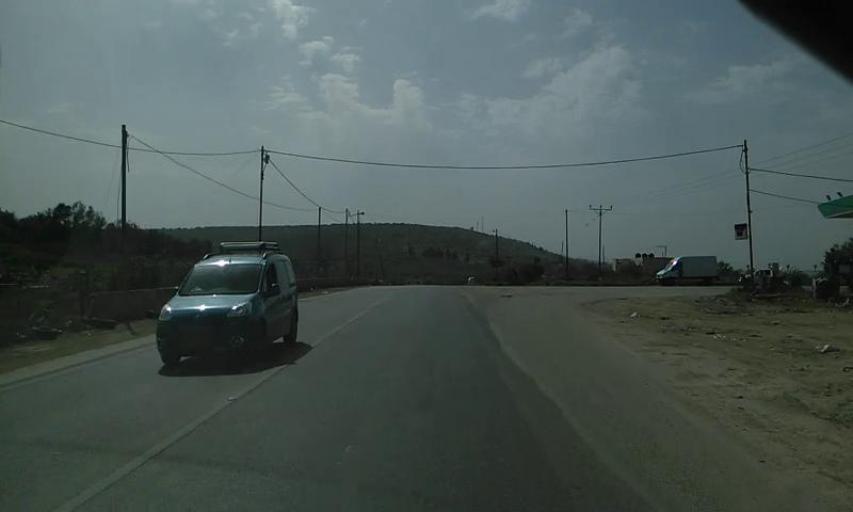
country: PS
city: Bir al Basha
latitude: 32.4252
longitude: 35.2503
